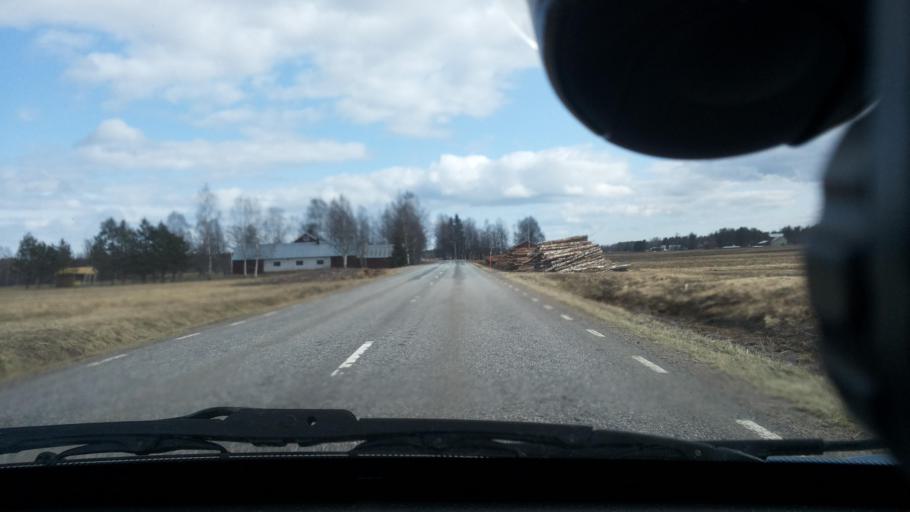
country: SE
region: Norrbotten
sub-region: Lulea Kommun
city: Sodra Sunderbyn
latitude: 65.6565
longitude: 21.8469
